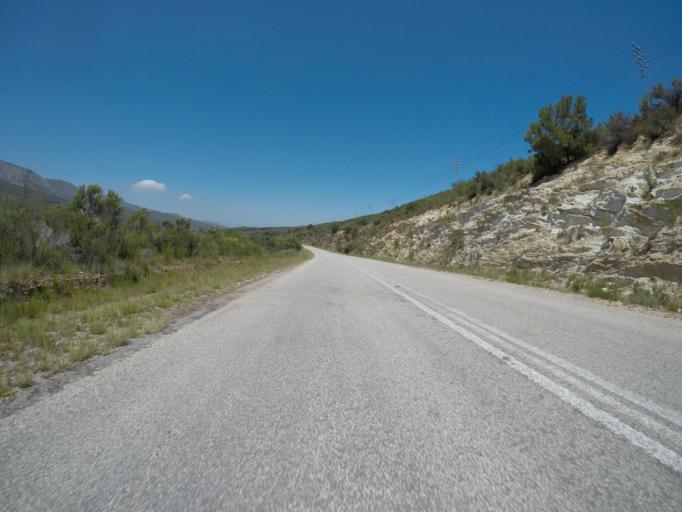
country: ZA
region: Eastern Cape
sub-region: Cacadu District Municipality
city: Kareedouw
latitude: -33.9118
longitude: 24.1680
